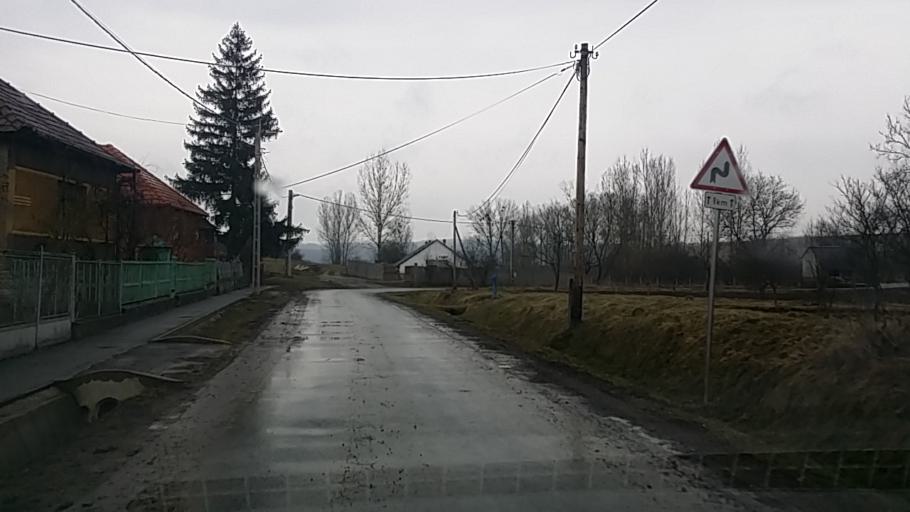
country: HU
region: Borsod-Abauj-Zemplen
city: Rudabanya
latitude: 48.4418
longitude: 20.5898
